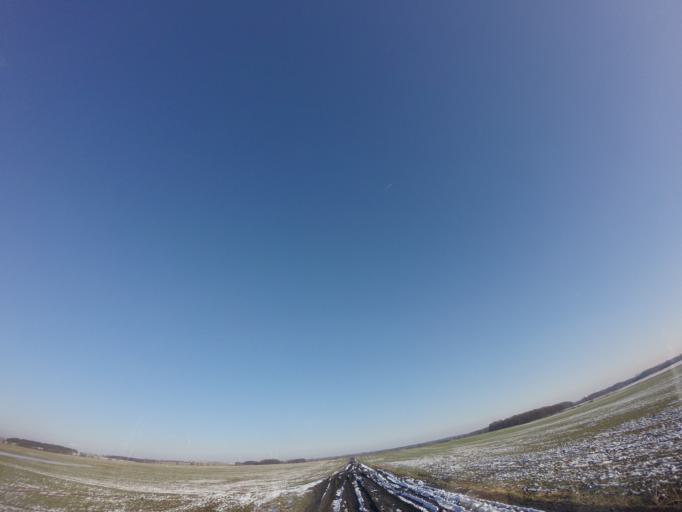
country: PL
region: West Pomeranian Voivodeship
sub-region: Powiat choszczenski
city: Choszczno
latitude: 53.0991
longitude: 15.3708
